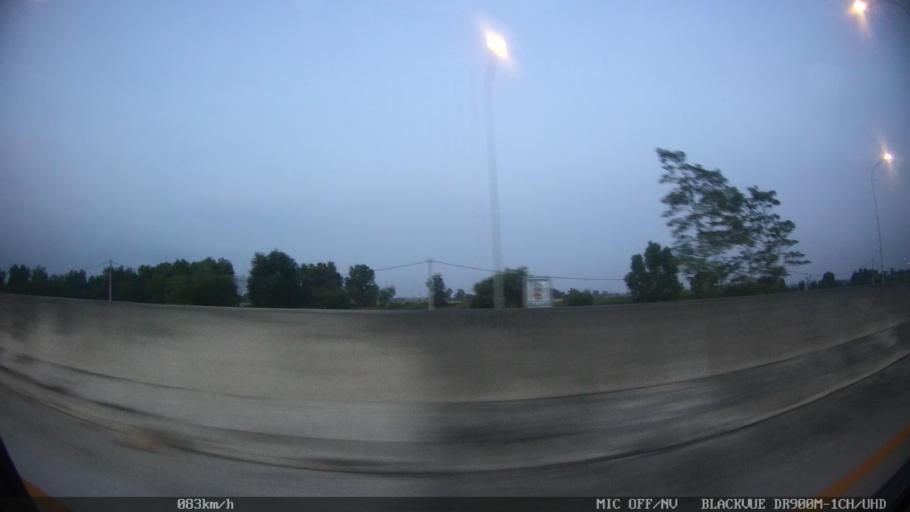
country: ID
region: Lampung
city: Sidorejo
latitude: -5.6050
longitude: 105.5555
